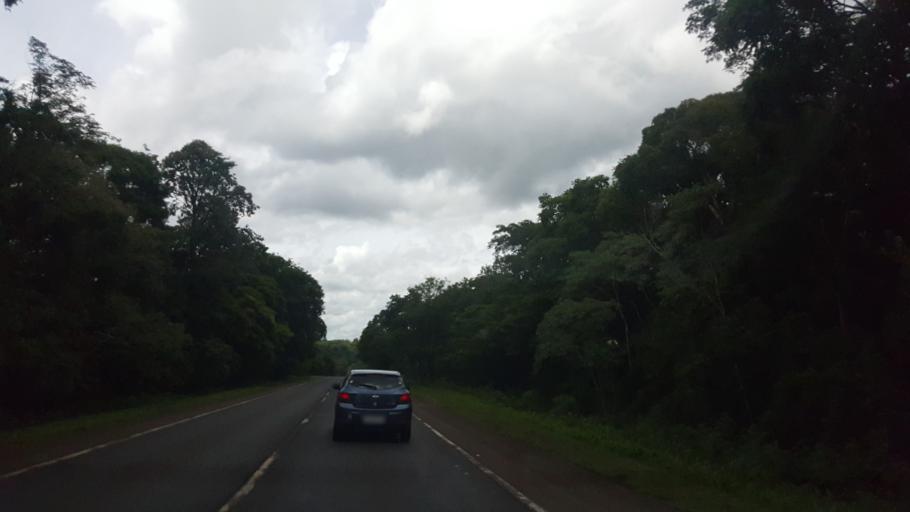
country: AR
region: Misiones
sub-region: Departamento de Iguazu
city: Puerto Iguazu
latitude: -25.6861
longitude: -54.5118
